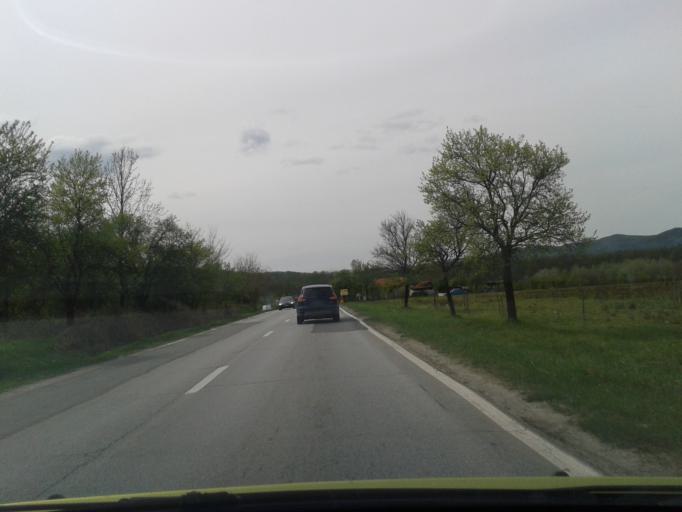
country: RO
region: Hunedoara
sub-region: Comuna Dobra
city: Dobra
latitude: 45.9109
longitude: 22.5431
